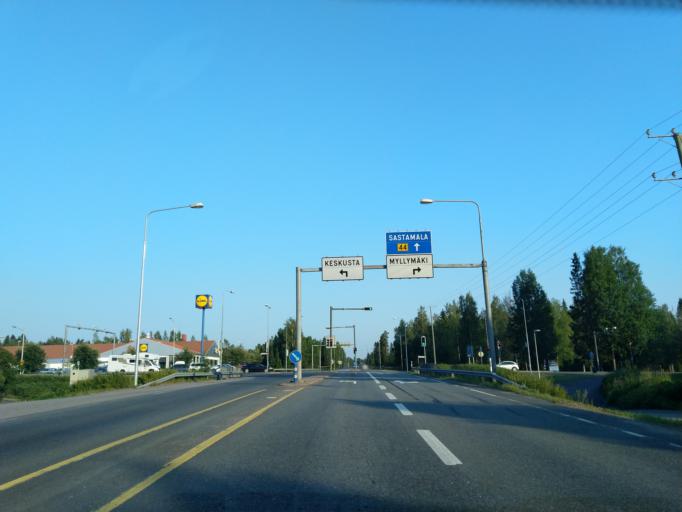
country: FI
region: Satakunta
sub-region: Pohjois-Satakunta
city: Kankaanpaeae
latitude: 61.8133
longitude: 22.3743
